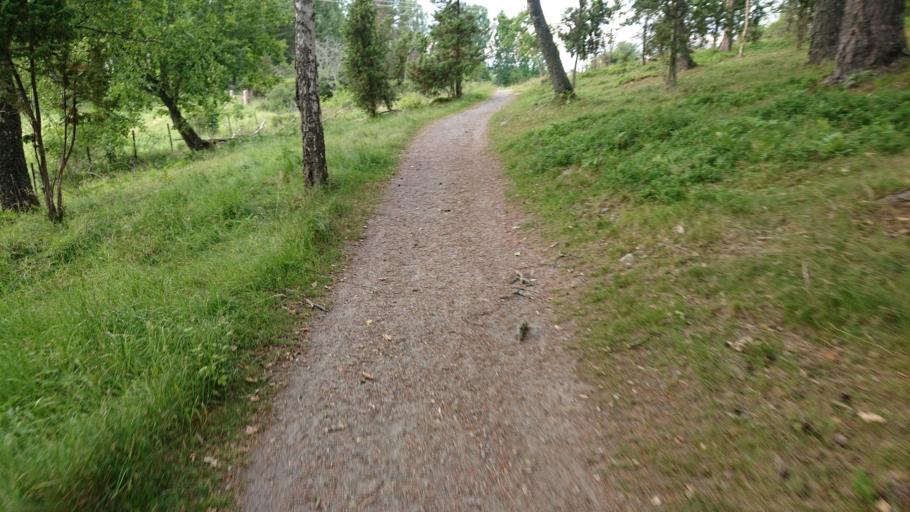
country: SE
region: Stockholm
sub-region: Osterakers Kommun
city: Akersberga
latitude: 59.4953
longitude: 18.2970
